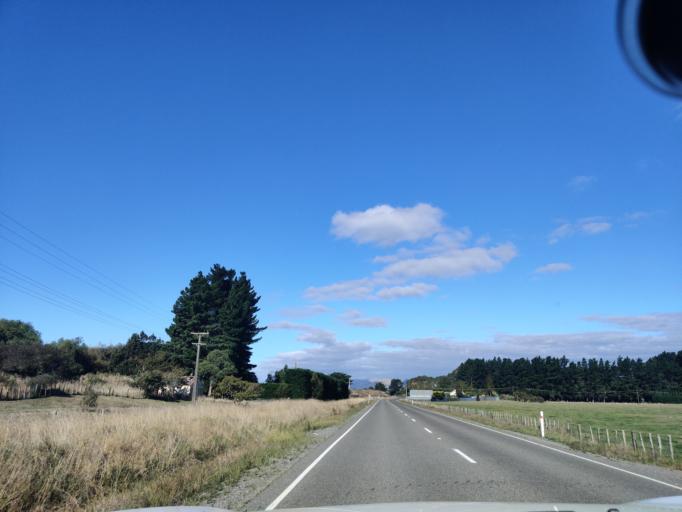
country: NZ
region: Manawatu-Wanganui
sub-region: Horowhenua District
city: Foxton
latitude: -40.4202
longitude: 175.4315
